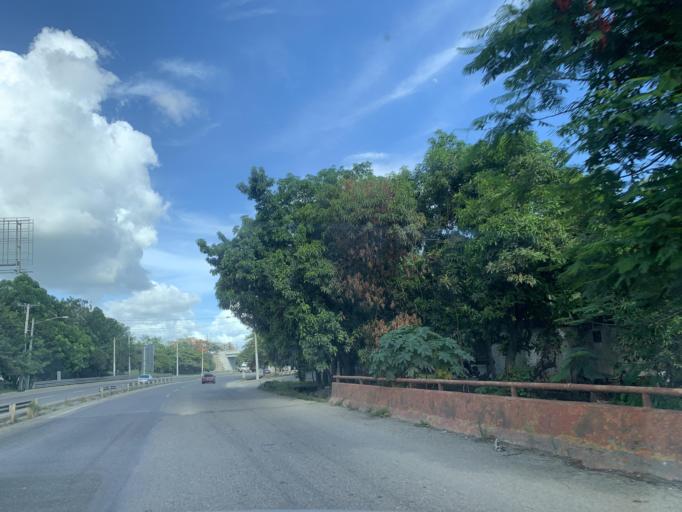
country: DO
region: Santiago
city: Villa Gonzalez
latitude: 19.5346
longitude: -70.7841
